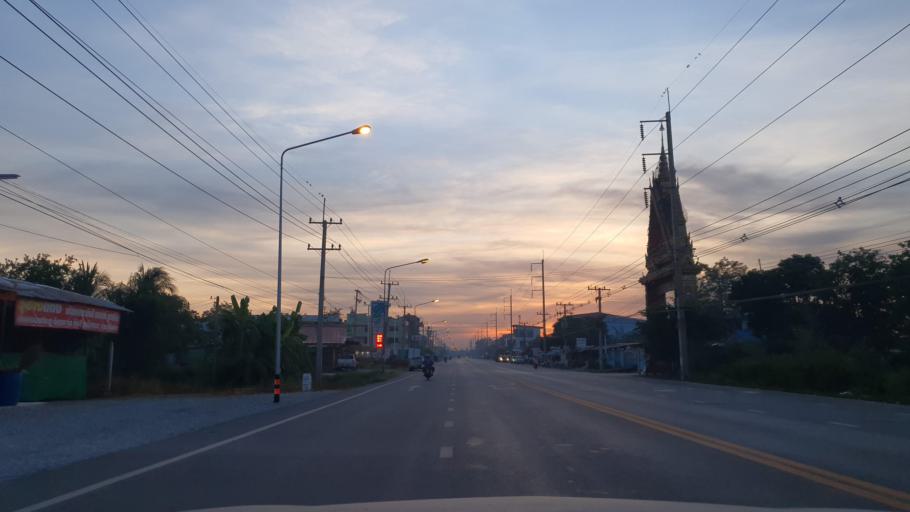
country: TH
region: Nakhon Sawan
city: Kao Liao
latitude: 15.7679
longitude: 99.9798
